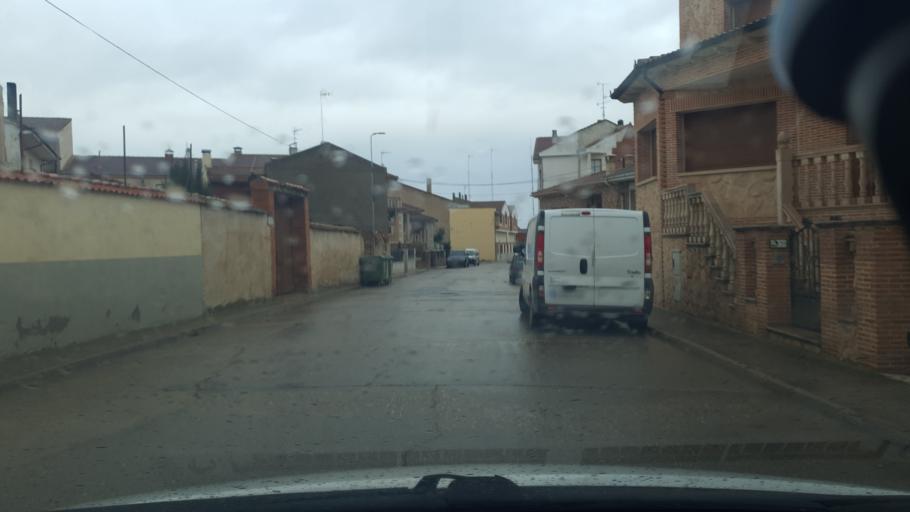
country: ES
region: Castille and Leon
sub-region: Provincia de Segovia
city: Carbonero el Mayor
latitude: 41.1190
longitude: -4.2642
